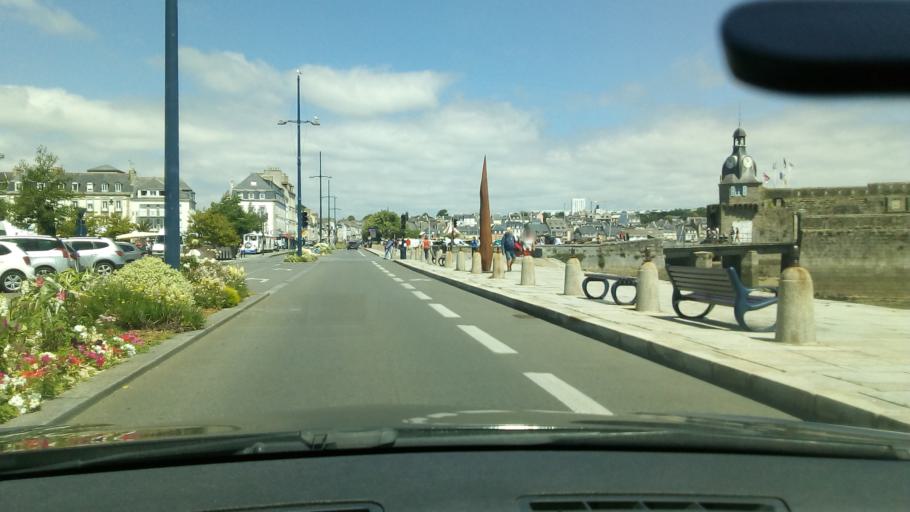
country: FR
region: Brittany
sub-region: Departement du Finistere
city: Concarneau
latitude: 47.8708
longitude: -3.9167
